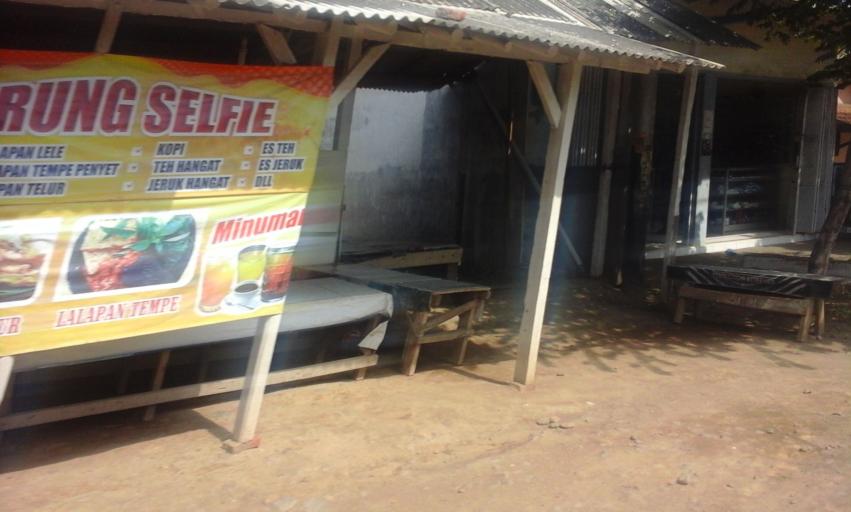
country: ID
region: East Java
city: Klatakan
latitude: -8.1540
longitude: 114.3961
